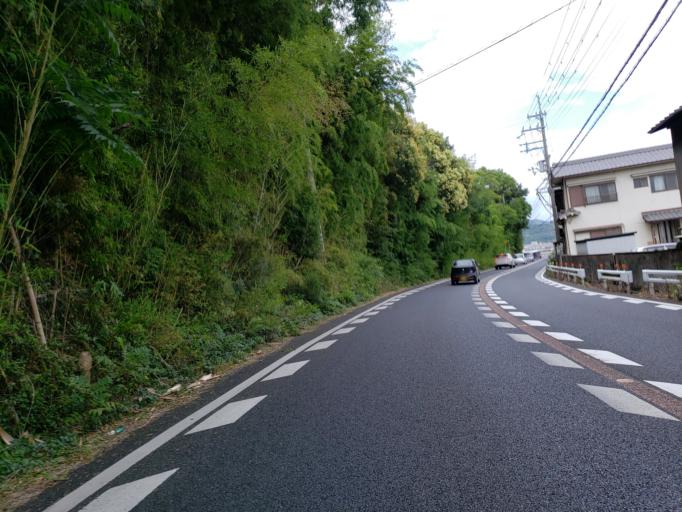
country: JP
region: Hyogo
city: Shirahamacho-usazakiminami
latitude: 34.7769
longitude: 134.7701
